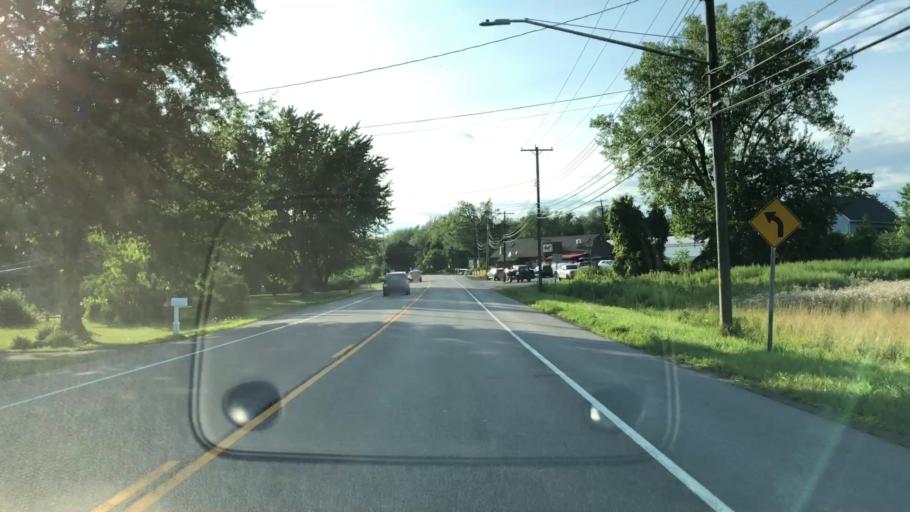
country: US
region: New York
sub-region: Erie County
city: West Seneca
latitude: 42.8671
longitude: -78.7745
